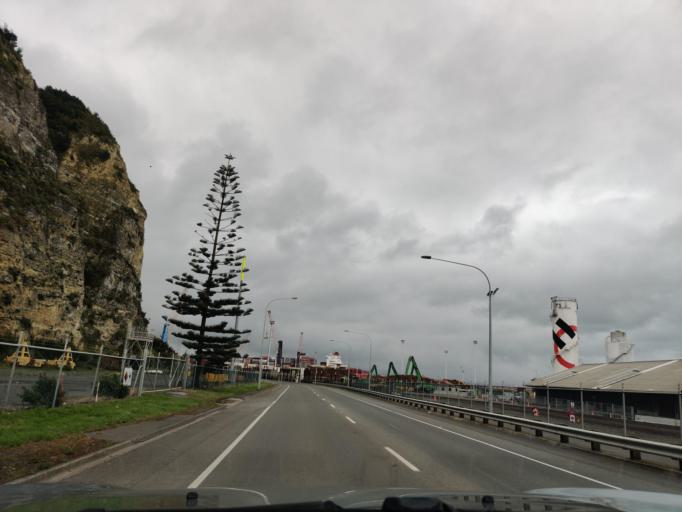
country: NZ
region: Hawke's Bay
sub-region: Napier City
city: Napier
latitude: -39.4796
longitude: 176.9208
